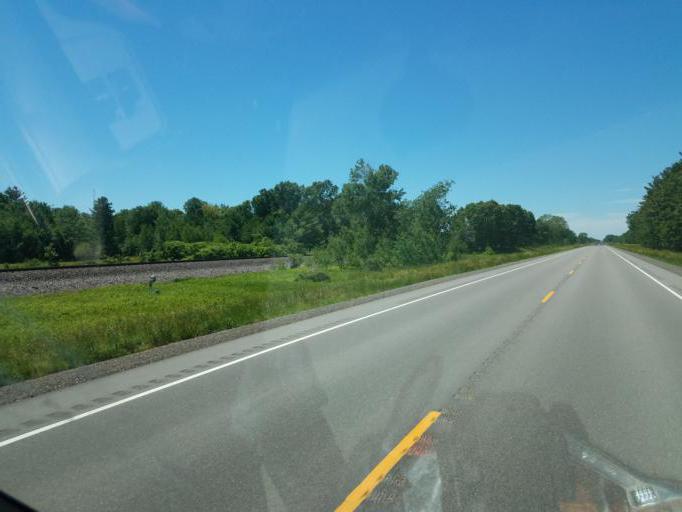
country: US
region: Wisconsin
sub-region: Juneau County
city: New Lisbon
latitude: 44.0250
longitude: -90.1463
